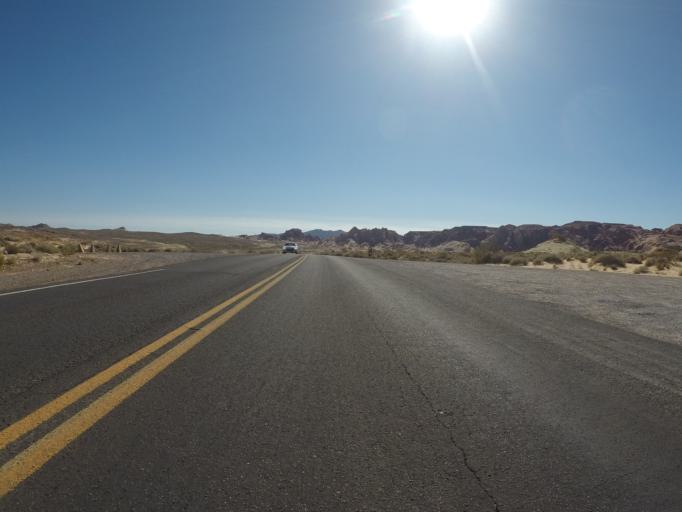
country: US
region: Nevada
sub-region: Clark County
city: Moapa Valley
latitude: 36.4720
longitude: -114.5264
